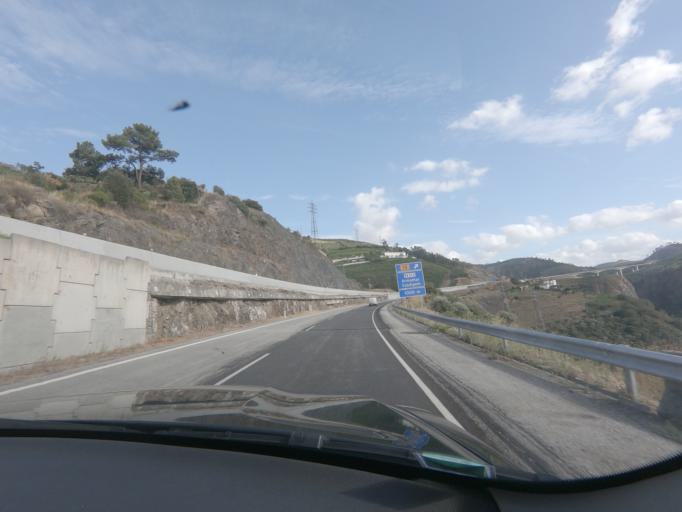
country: PT
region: Vila Real
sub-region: Peso da Regua
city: Peso da Regua
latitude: 41.1426
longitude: -7.7737
